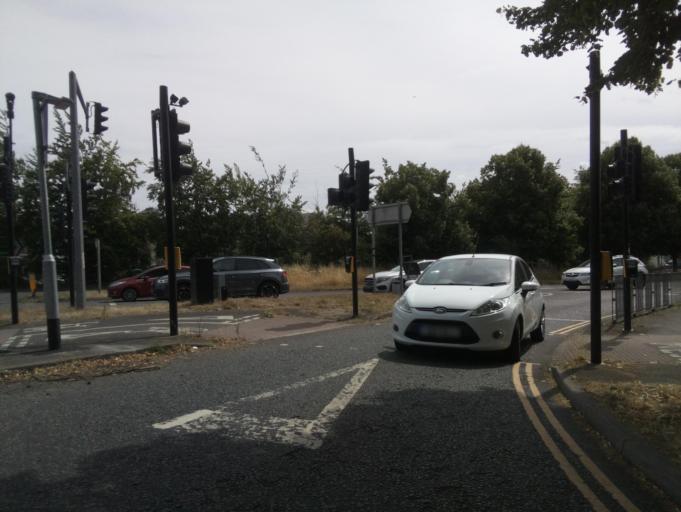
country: GB
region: England
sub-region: Surrey
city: Dorking
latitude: 51.2406
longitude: -0.3259
